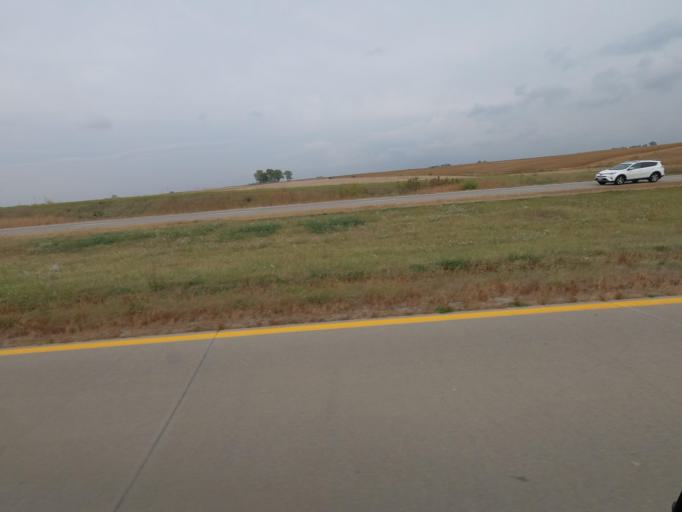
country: US
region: Iowa
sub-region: Mahaska County
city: Oskaloosa
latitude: 41.3315
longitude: -92.7203
